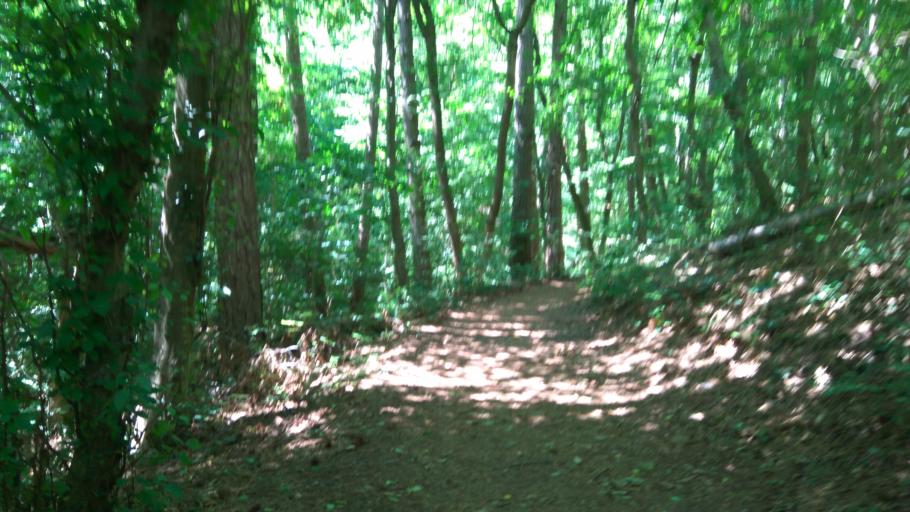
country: HU
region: Veszprem
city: Balatonfured
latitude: 46.9916
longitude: 17.8842
